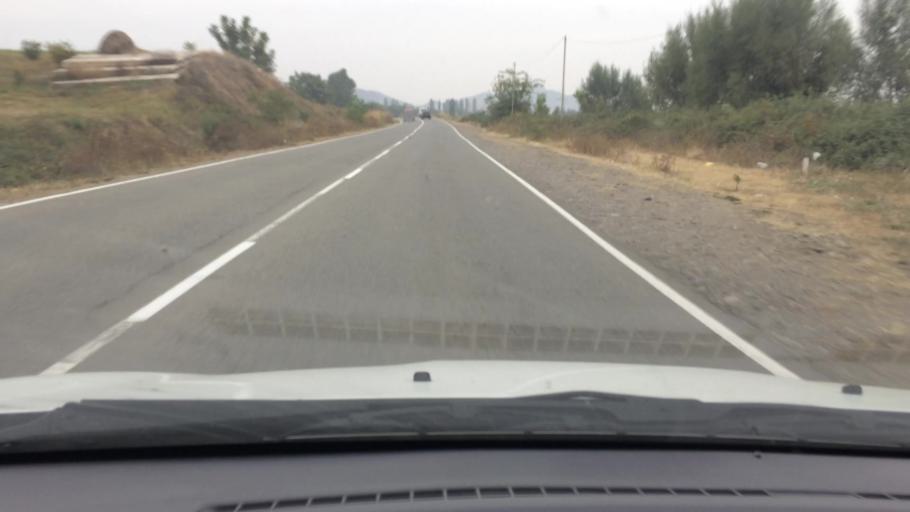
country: GE
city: Naghvarevi
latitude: 41.3121
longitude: 44.7925
